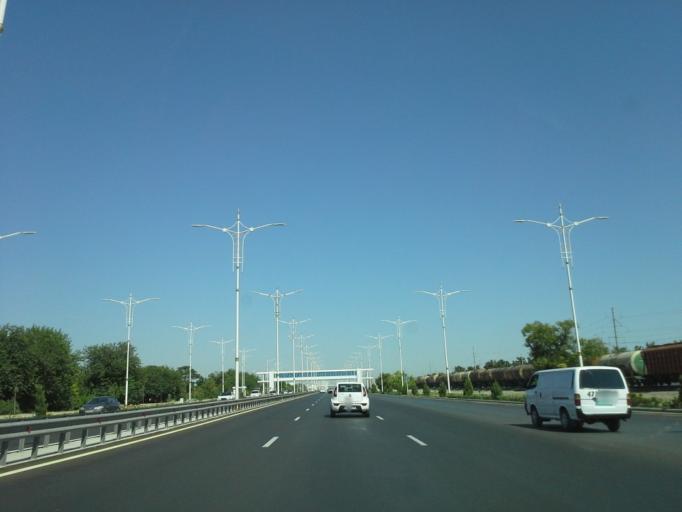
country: TM
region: Ahal
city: Ashgabat
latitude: 37.9680
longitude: 58.3553
